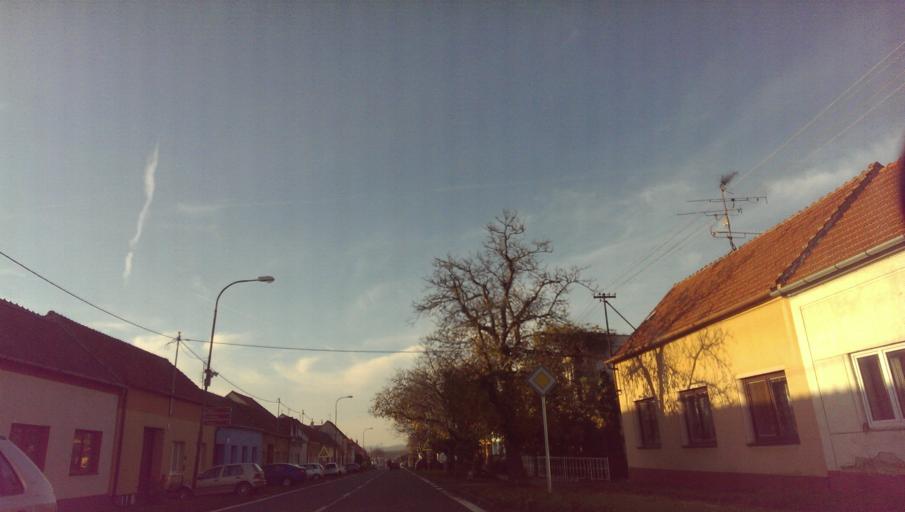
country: CZ
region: Zlin
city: Uhersky Ostroh
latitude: 48.9837
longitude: 17.4085
